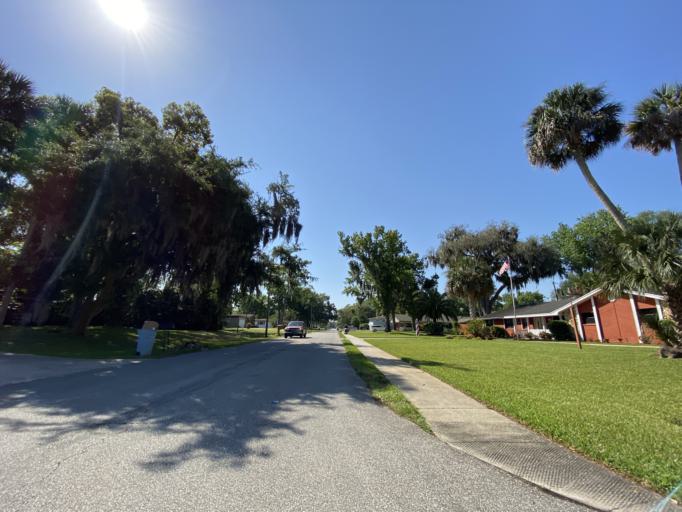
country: US
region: Florida
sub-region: Volusia County
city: South Daytona
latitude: 29.1646
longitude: -81.0125
